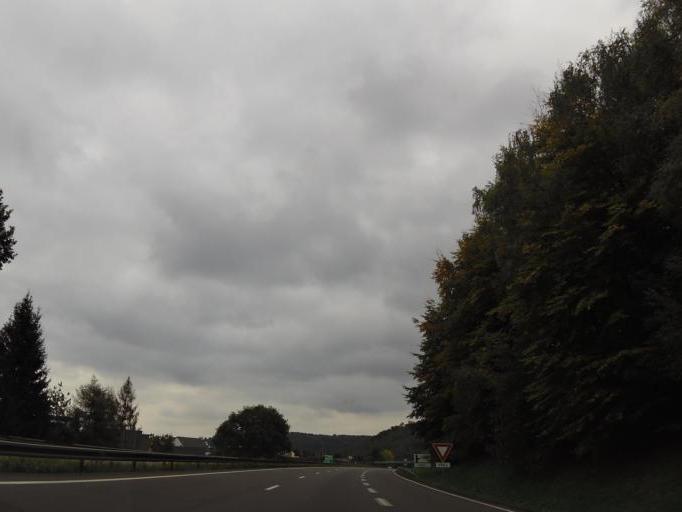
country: FR
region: Lorraine
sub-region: Departement de la Moselle
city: Morsbach
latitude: 49.1642
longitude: 6.8631
